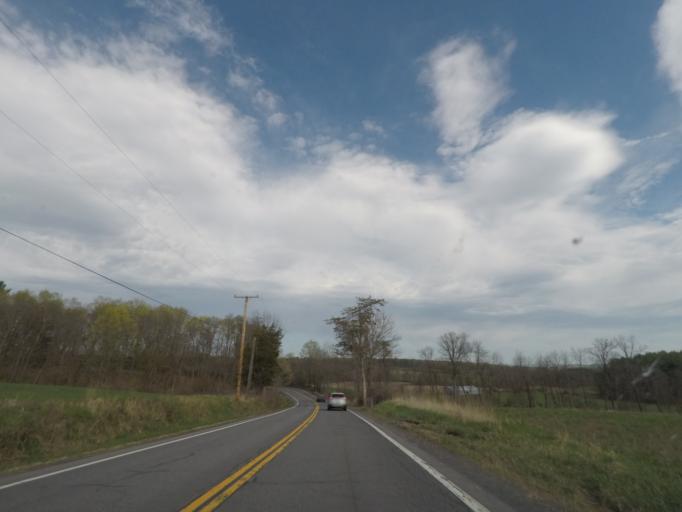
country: US
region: New York
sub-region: Albany County
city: Voorheesville
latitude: 42.5684
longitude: -73.9063
